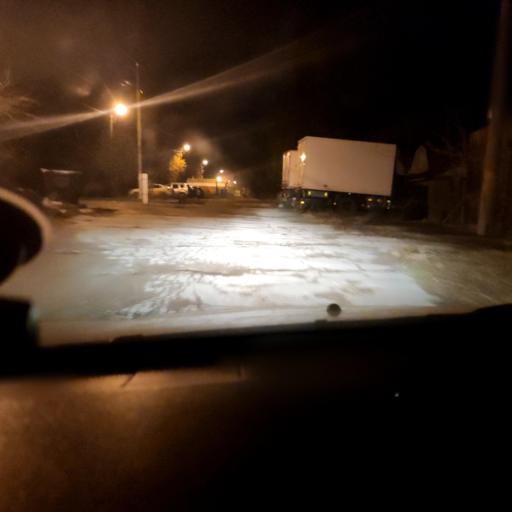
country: RU
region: Samara
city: Petra-Dubrava
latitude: 53.2605
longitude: 50.3235
